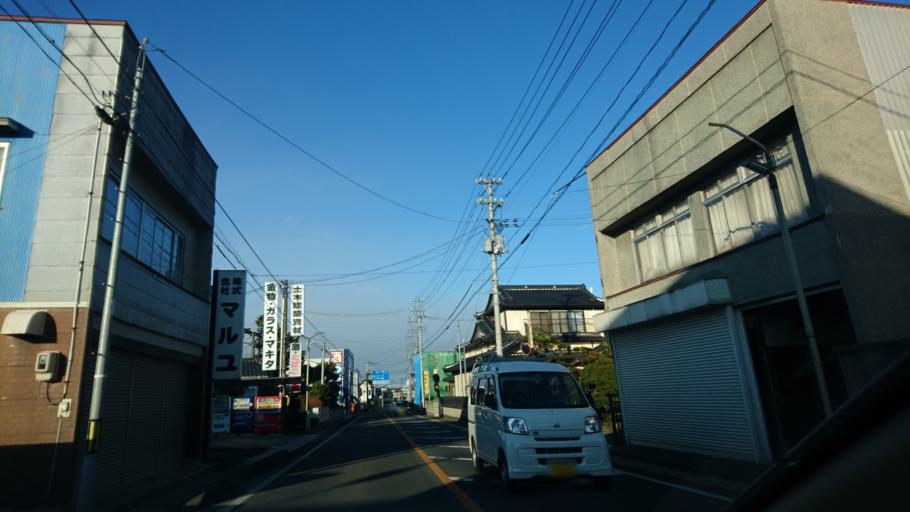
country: JP
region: Miyagi
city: Furukawa
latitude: 38.5460
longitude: 140.8510
